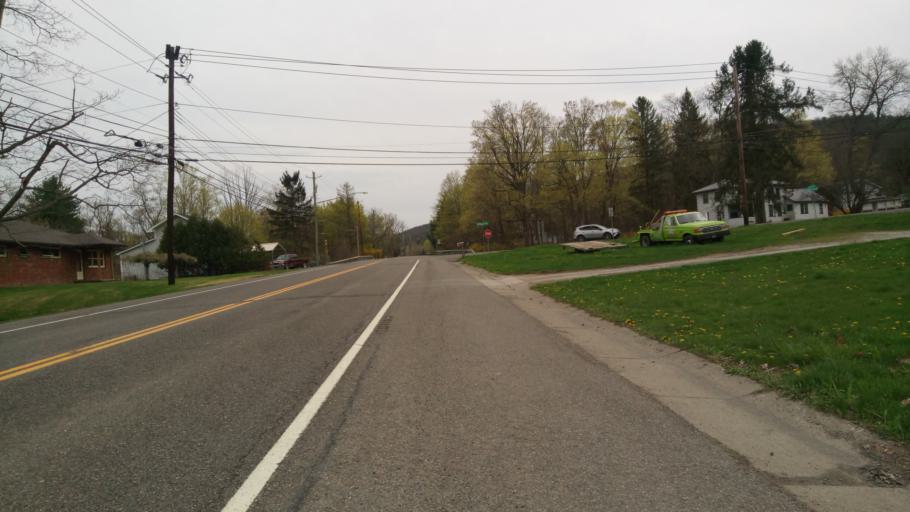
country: US
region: New York
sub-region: Chemung County
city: Southport
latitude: 42.0069
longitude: -76.7297
